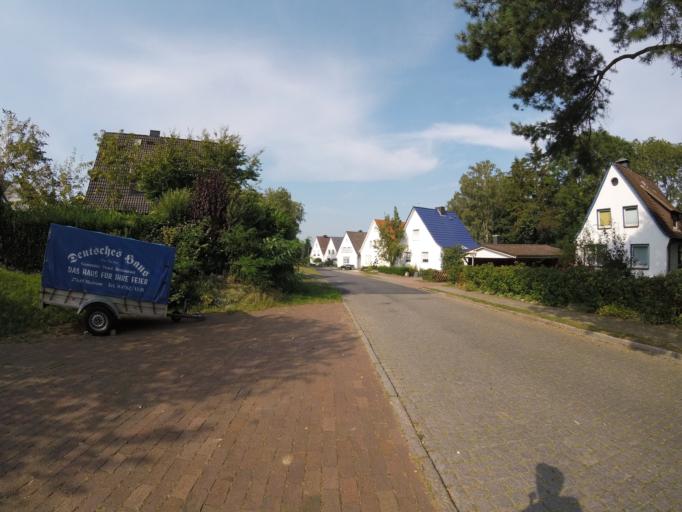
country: DE
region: Lower Saxony
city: Stade
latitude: 53.6095
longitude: 9.4615
